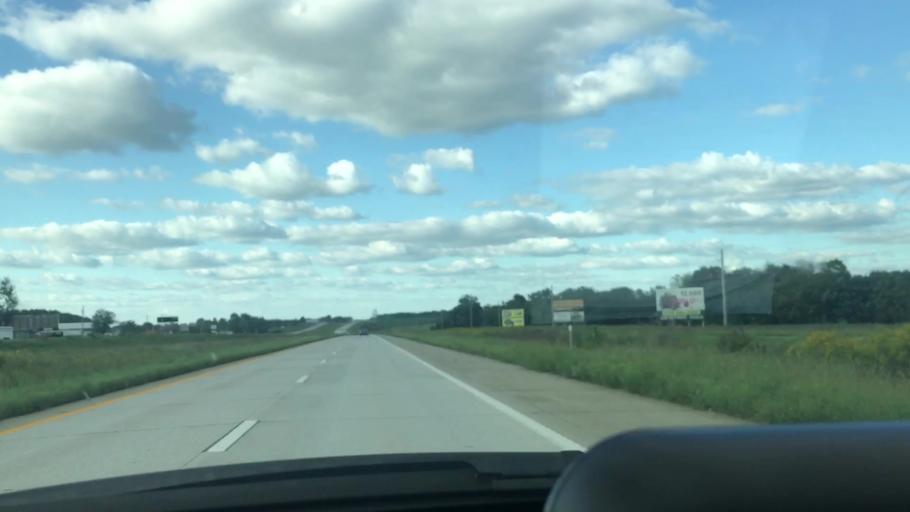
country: US
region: Missouri
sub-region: Benton County
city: Cole Camp
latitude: 38.5201
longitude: -93.2723
